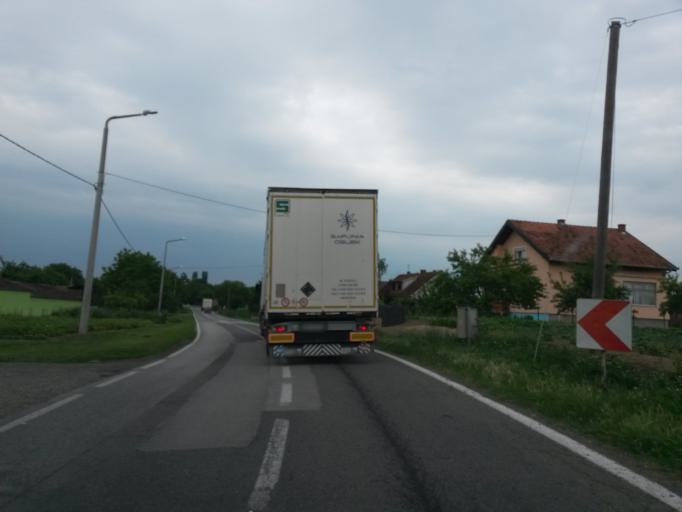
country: HR
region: Vukovarsko-Srijemska
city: Lovas
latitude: 45.2887
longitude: 19.1125
